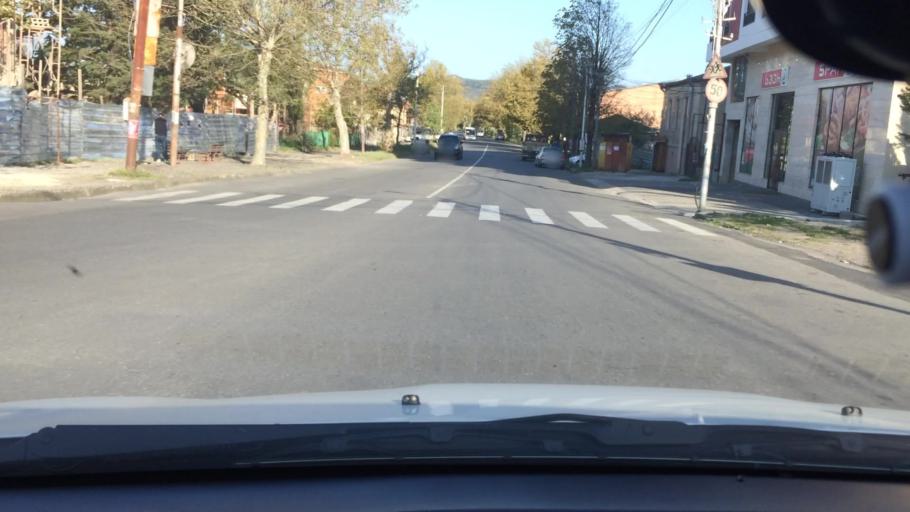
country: GE
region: Imereti
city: Kutaisi
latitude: 42.2664
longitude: 42.7181
